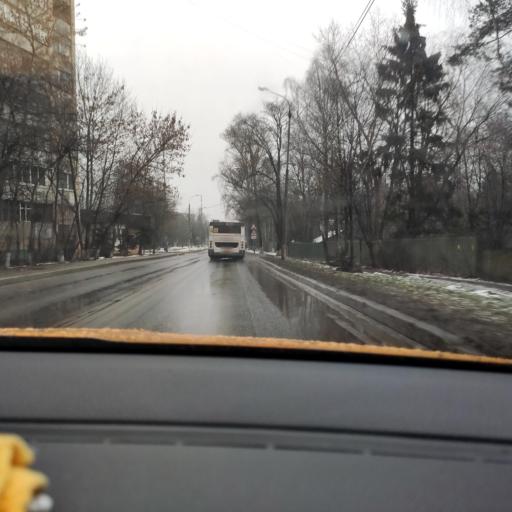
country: RU
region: Moskovskaya
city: Domodedovo
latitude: 55.4220
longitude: 37.7683
